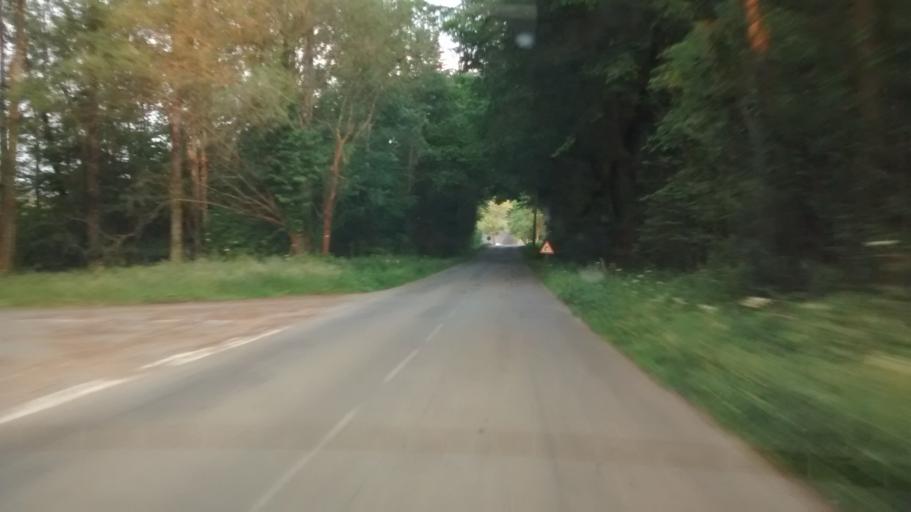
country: FR
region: Brittany
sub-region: Departement du Morbihan
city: Beignon
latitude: 47.9958
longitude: -2.1433
